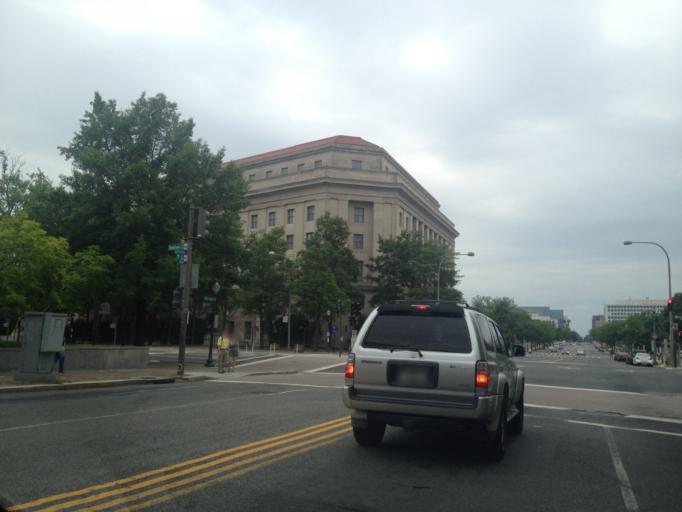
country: US
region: Washington, D.C.
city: Washington, D.C.
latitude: 38.8938
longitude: -77.0218
